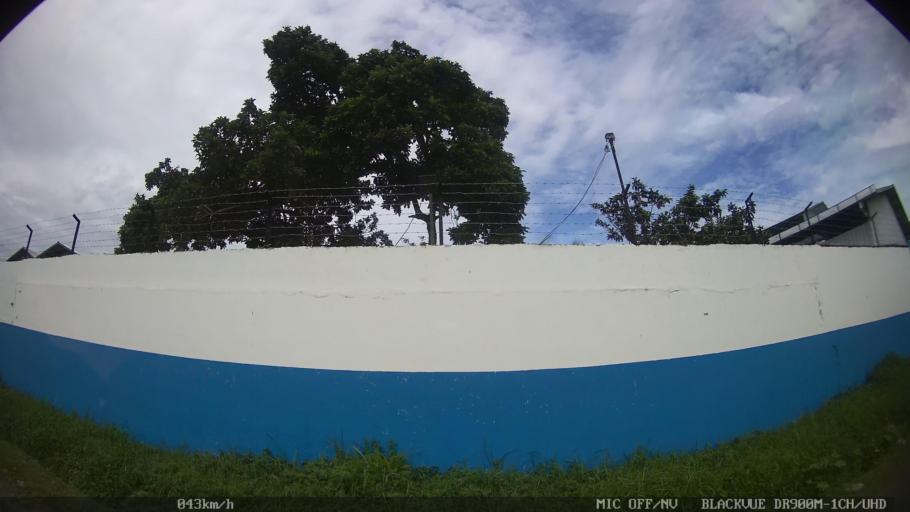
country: ID
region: North Sumatra
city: Sunggal
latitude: 3.5865
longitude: 98.5775
